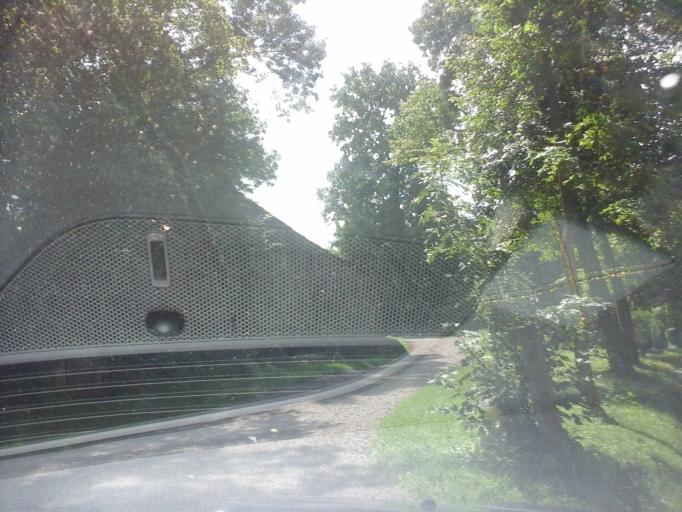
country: PL
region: Lesser Poland Voivodeship
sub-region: Powiat wadowicki
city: Ryczow
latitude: 49.9802
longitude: 19.5604
